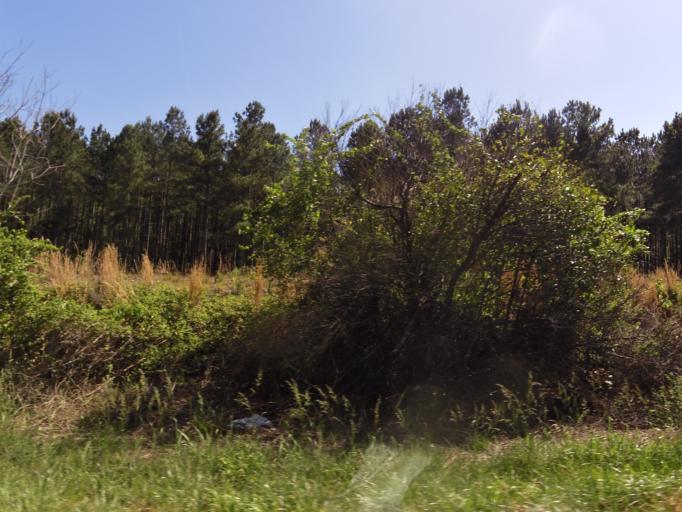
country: US
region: South Carolina
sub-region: Aiken County
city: Aiken
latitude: 33.5220
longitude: -81.6105
